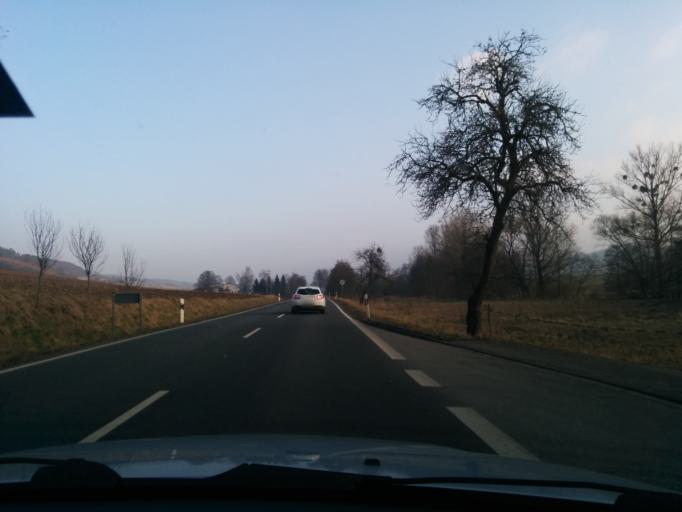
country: DE
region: Hesse
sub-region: Regierungsbezirk Kassel
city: Weissenborn
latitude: 51.1053
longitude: 10.0601
